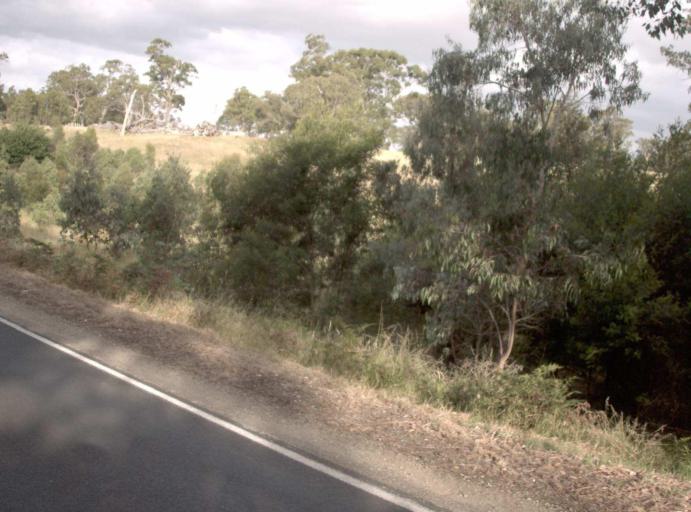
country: AU
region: Victoria
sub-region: Wellington
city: Sale
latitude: -37.9252
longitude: 146.9959
